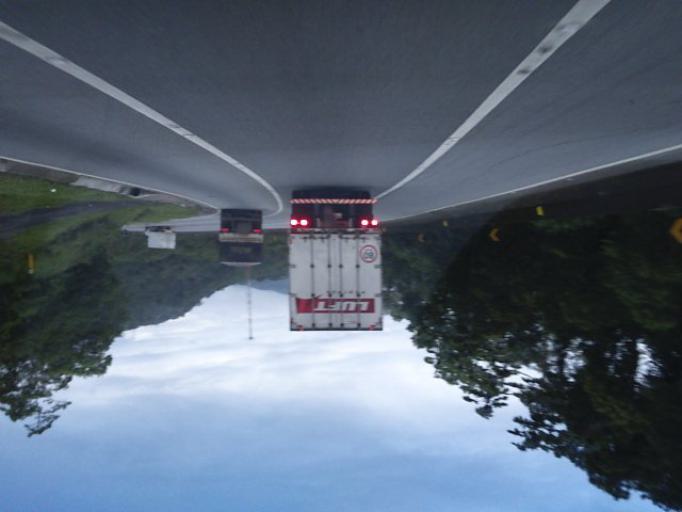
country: BR
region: Parana
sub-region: Guaratuba
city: Guaratuba
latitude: -25.8643
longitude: -48.9499
